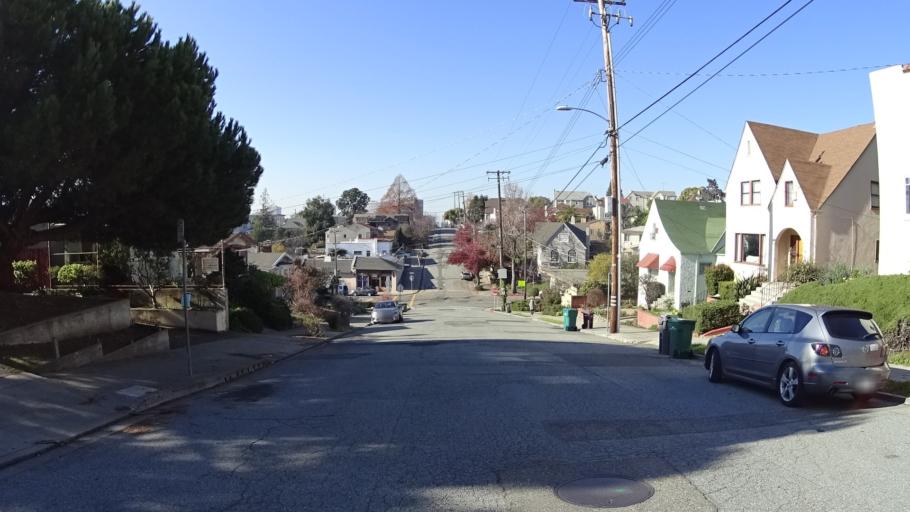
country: US
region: California
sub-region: Alameda County
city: Piedmont
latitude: 37.8044
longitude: -122.2439
